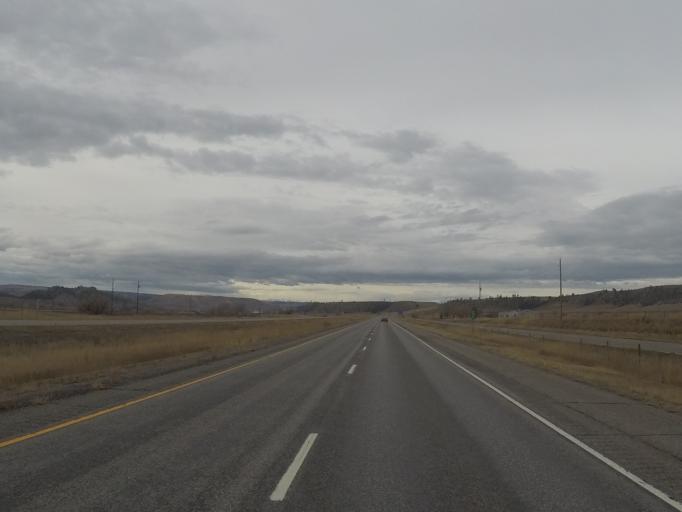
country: US
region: Montana
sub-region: Stillwater County
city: Columbus
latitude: 45.6085
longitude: -109.0223
